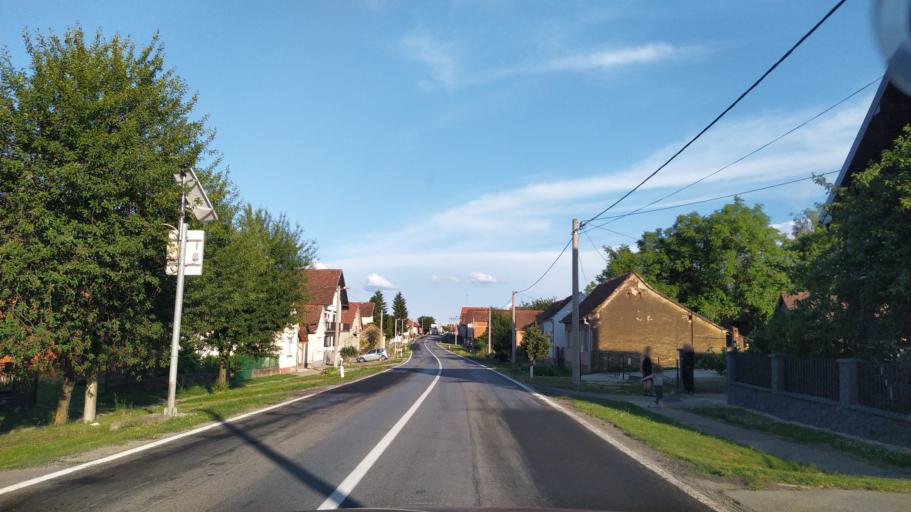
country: HR
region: Virovitick-Podravska
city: Slatina
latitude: 45.6875
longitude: 17.7340
